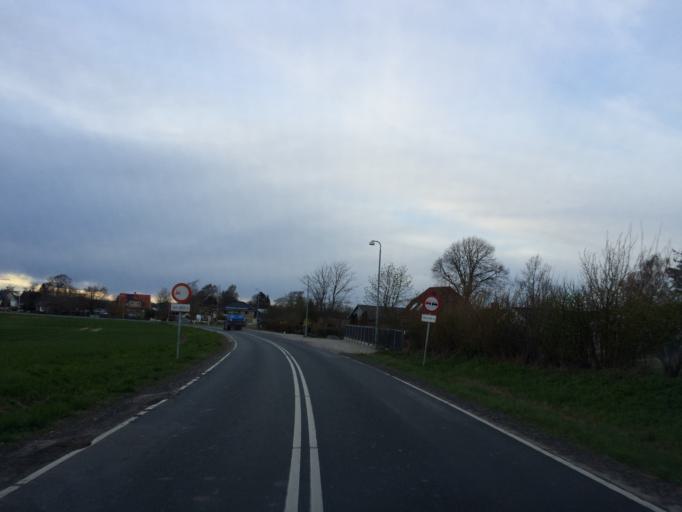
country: DK
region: South Denmark
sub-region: Odense Kommune
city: Bellinge
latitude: 55.3578
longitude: 10.2771
